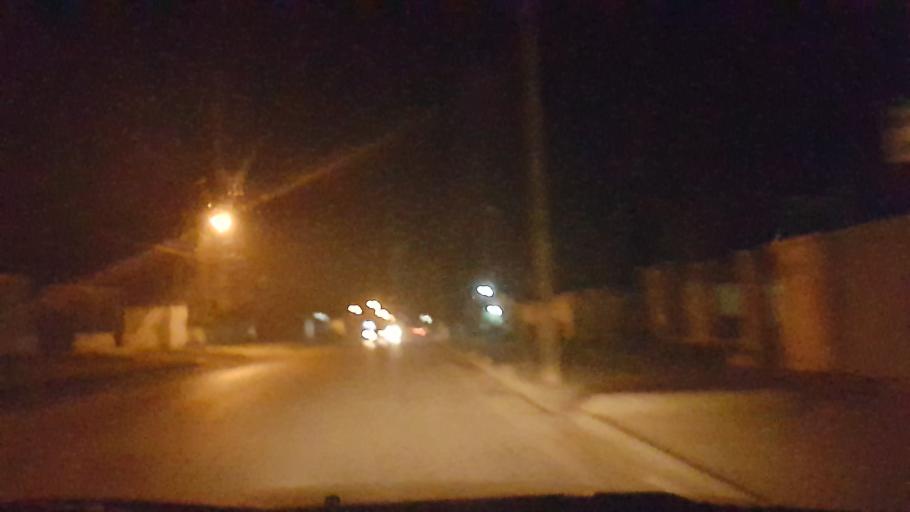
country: PY
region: Central
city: Colonia Mariano Roque Alonso
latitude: -25.1897
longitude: -57.5295
